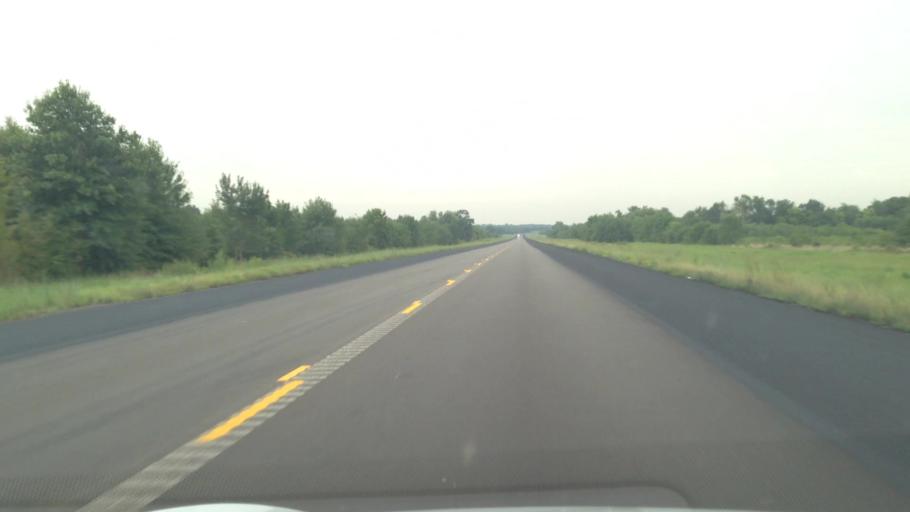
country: US
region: Kansas
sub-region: Cherokee County
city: Baxter Springs
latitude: 37.0424
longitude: -94.7108
